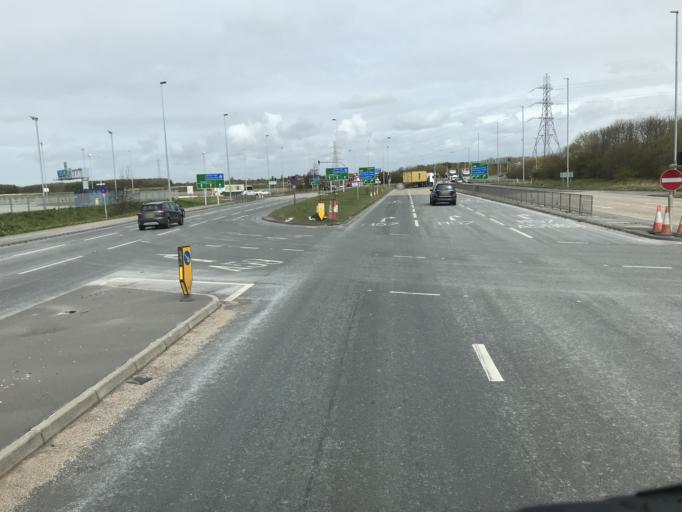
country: GB
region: England
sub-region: Sefton
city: Maghull
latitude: 53.4929
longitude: -2.9532
